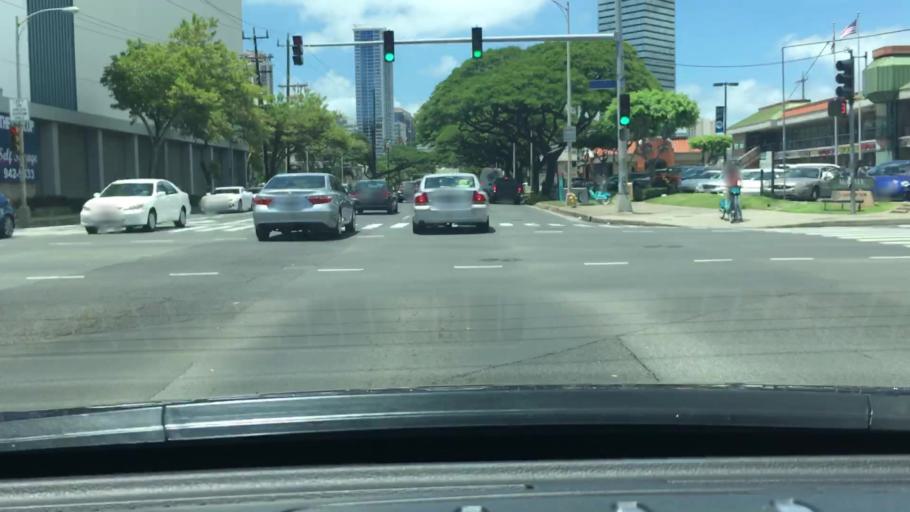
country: US
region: Hawaii
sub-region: Honolulu County
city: Honolulu
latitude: 21.2895
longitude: -157.8322
